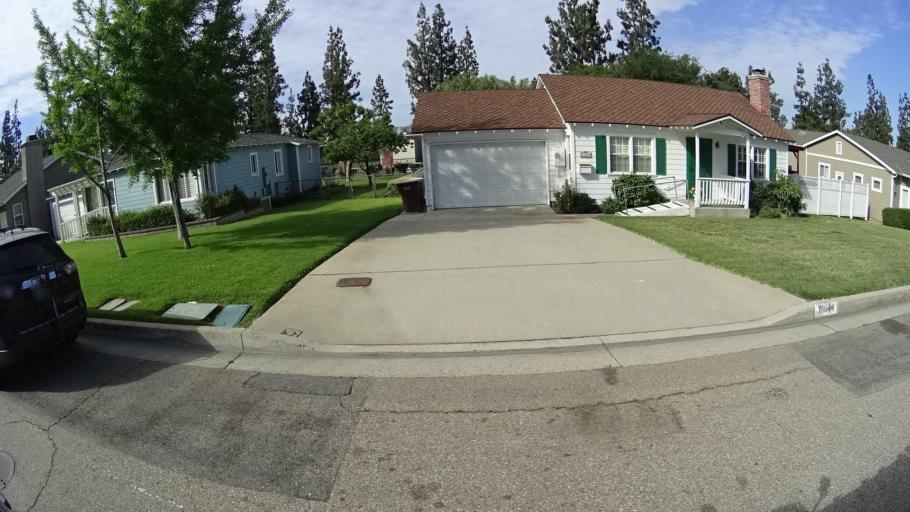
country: US
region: California
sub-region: Los Angeles County
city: La Puente
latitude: 34.0239
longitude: -117.9543
